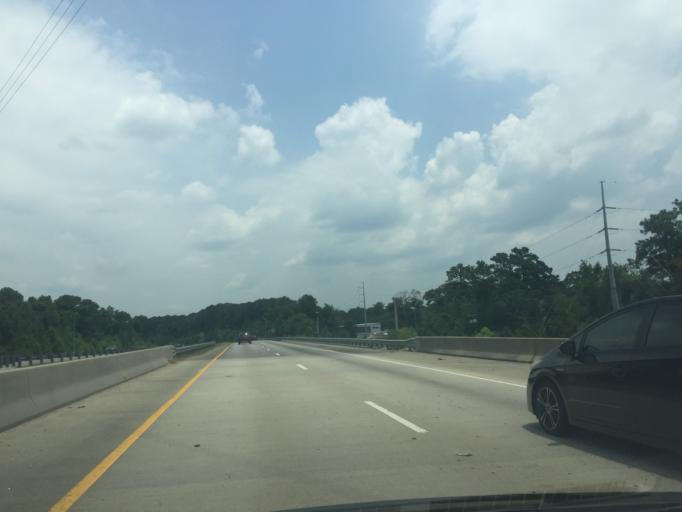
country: US
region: Georgia
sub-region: Chatham County
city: Isle of Hope
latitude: 32.0006
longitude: -81.0792
